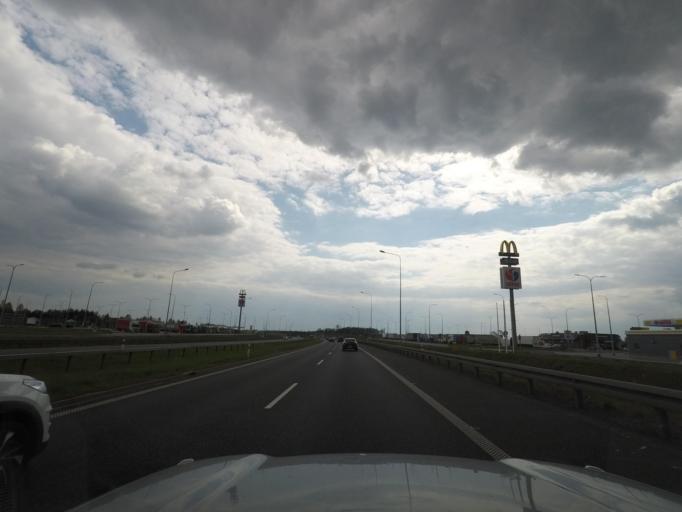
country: PL
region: Lower Silesian Voivodeship
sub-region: Legnica
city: Legnica
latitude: 51.2855
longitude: 16.1511
